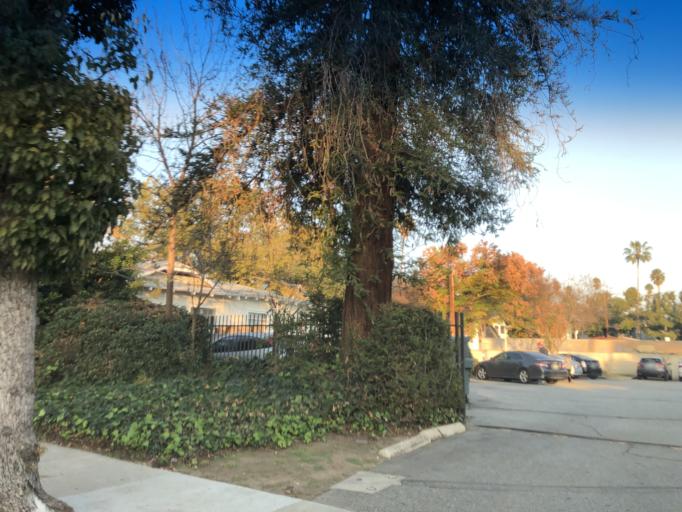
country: US
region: California
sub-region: Los Angeles County
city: East Pasadena
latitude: 34.1470
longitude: -118.1184
